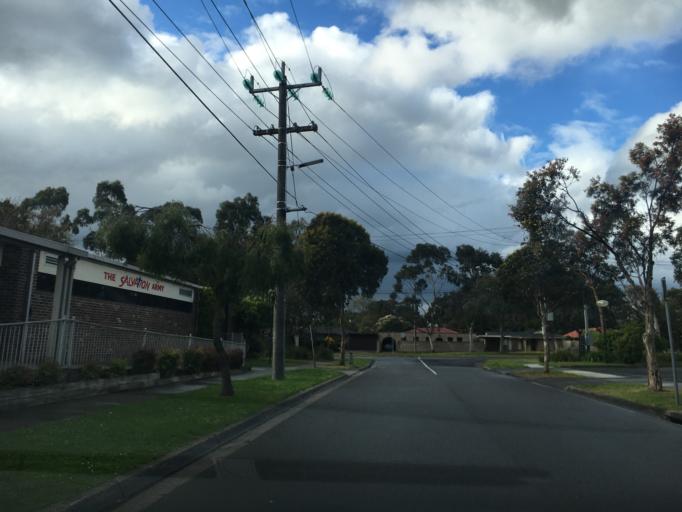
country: AU
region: Victoria
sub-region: Whitehorse
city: Vermont South
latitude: -37.8772
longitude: 145.1864
